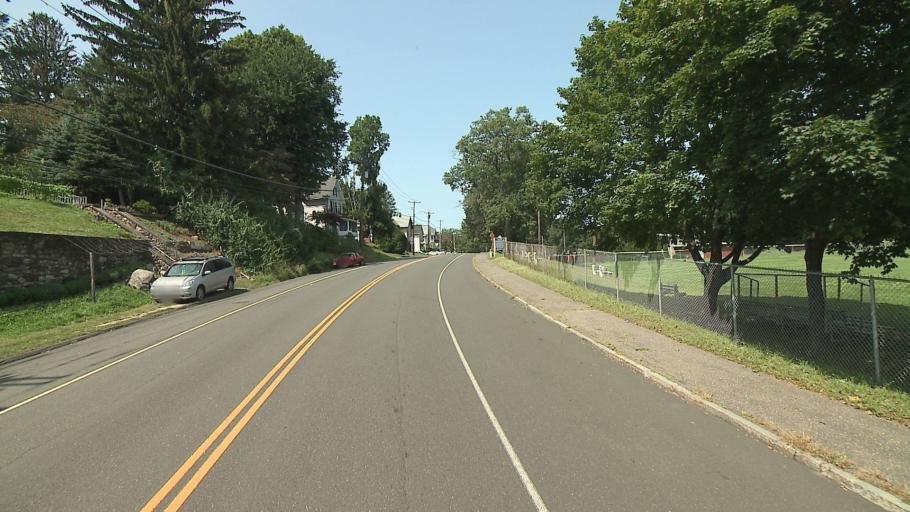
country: US
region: Connecticut
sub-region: Fairfield County
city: Shelton
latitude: 41.3212
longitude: -73.1005
